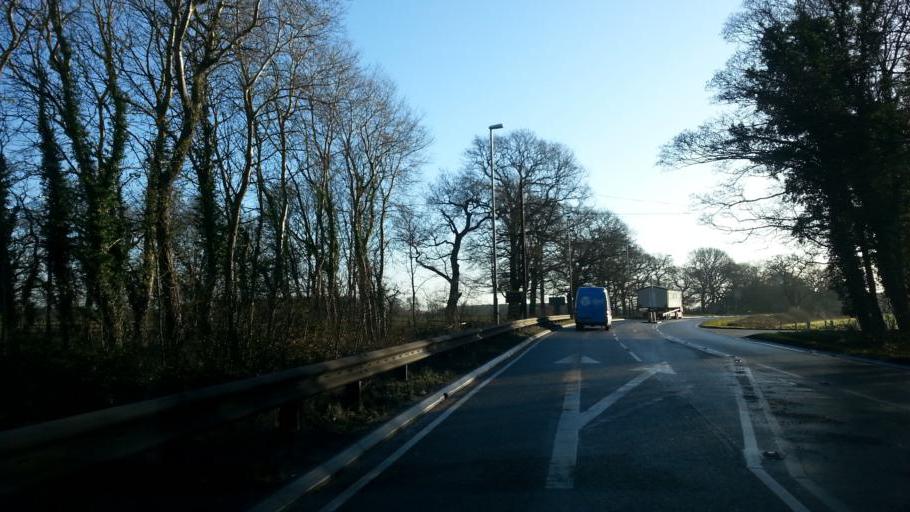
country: GB
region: England
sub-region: Nottinghamshire
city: South Collingham
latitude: 53.0822
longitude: -0.7279
